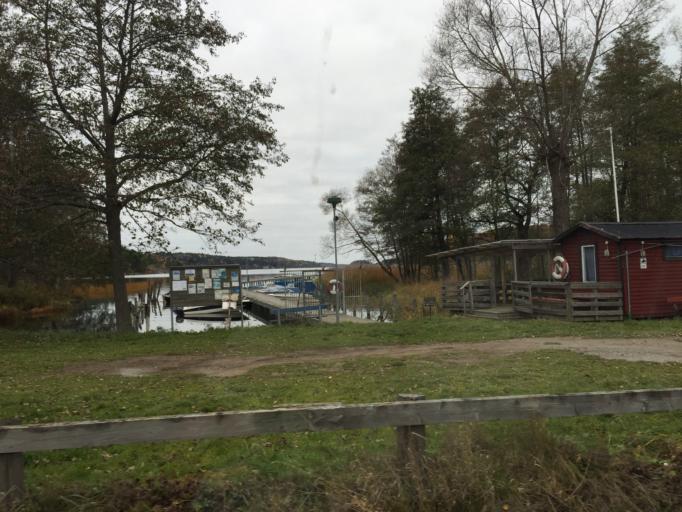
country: SE
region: Stockholm
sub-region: Sodertalje Kommun
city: Soedertaelje
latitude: 59.2478
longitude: 17.6112
